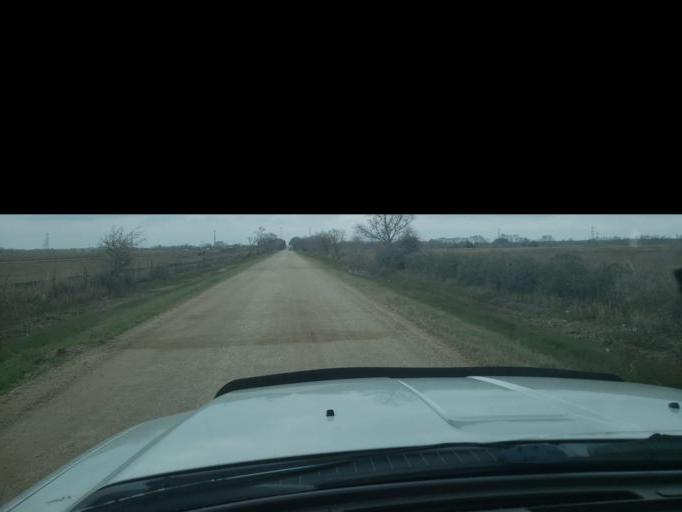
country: US
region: Texas
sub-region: Fort Bend County
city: Needville
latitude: 29.3543
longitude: -95.7595
